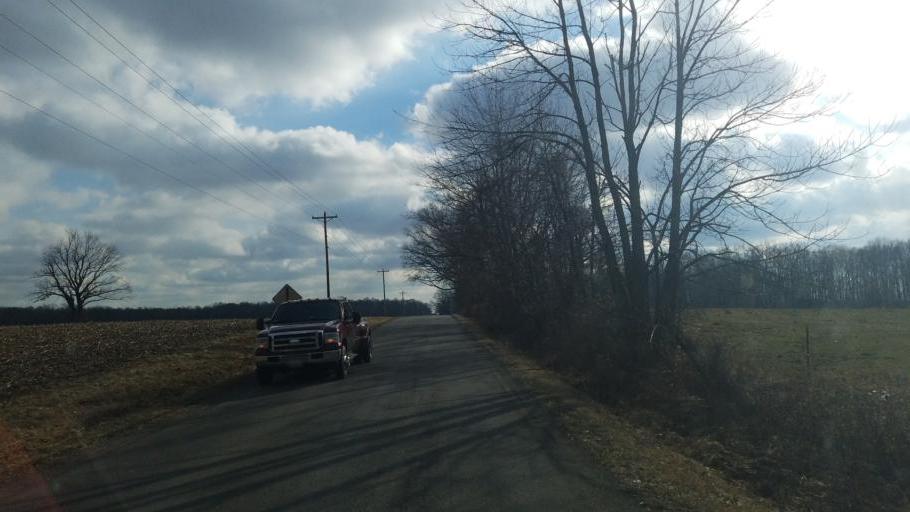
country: US
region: Ohio
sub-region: Morrow County
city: Mount Gilead
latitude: 40.5762
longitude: -82.7310
